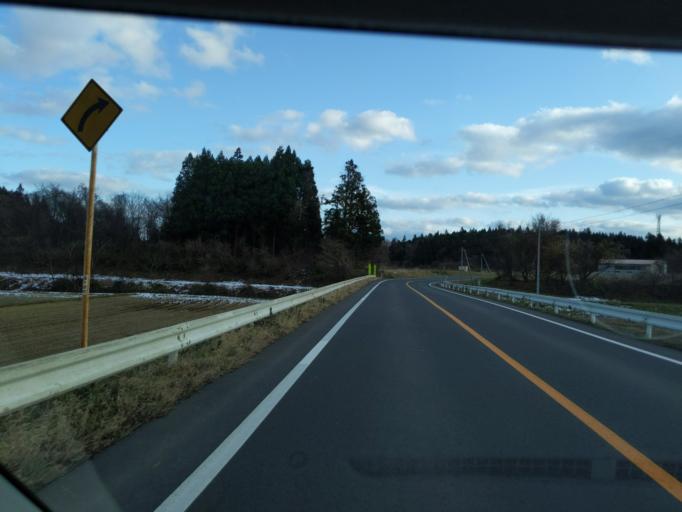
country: JP
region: Iwate
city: Mizusawa
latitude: 39.1617
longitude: 141.0519
